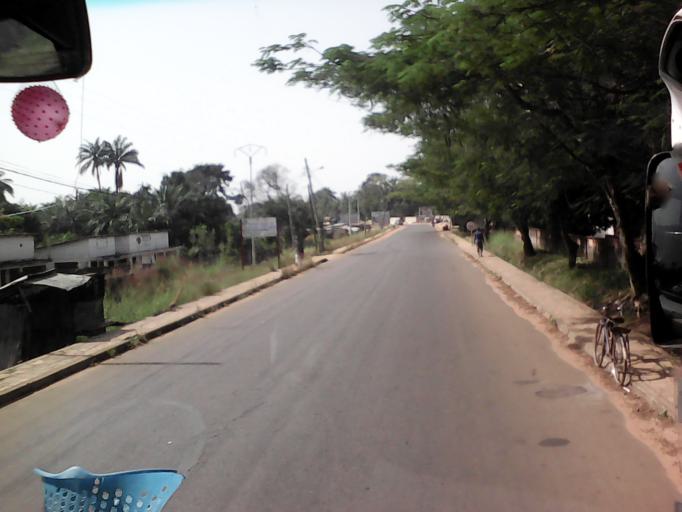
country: TG
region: Centrale
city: Sokode
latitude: 8.9710
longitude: 1.1372
